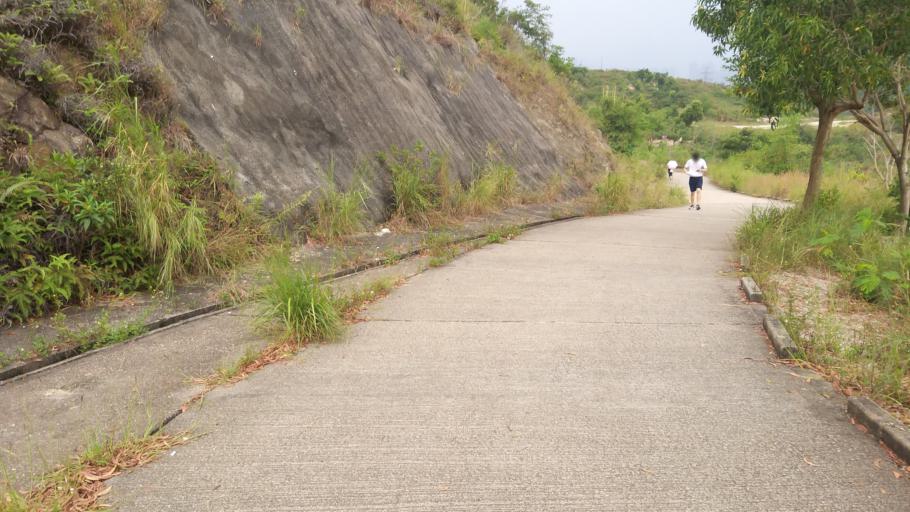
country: HK
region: Tuen Mun
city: Tuen Mun
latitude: 22.4085
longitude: 113.9523
